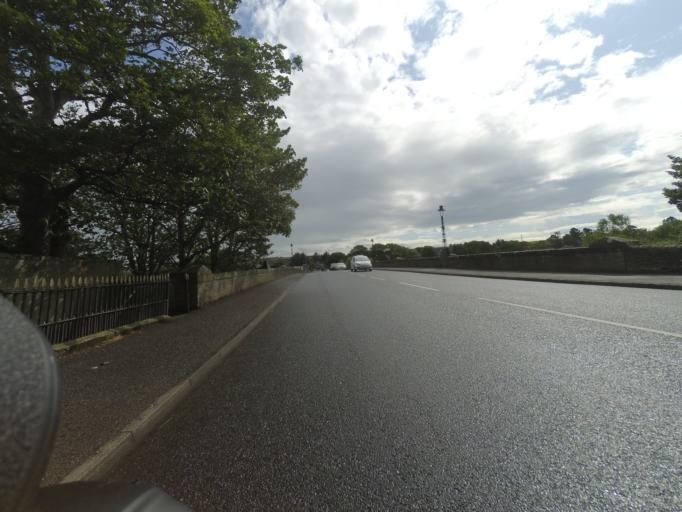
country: GB
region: Scotland
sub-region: Highland
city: Thurso
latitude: 58.5928
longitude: -3.5201
